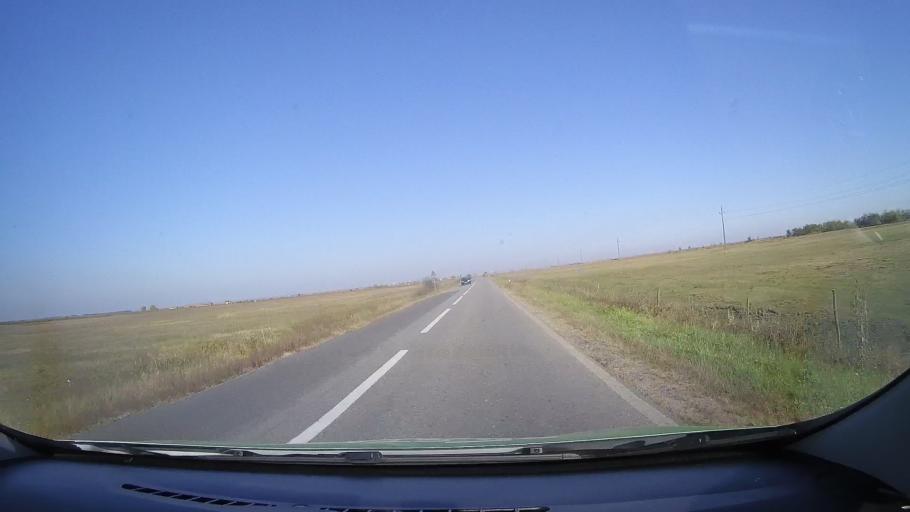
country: RO
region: Satu Mare
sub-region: Comuna Cauas
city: Cauas
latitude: 47.5426
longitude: 22.5639
